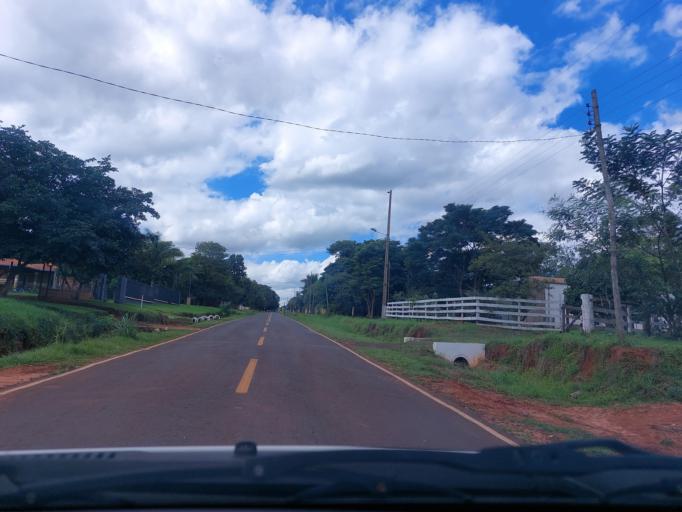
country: PY
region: San Pedro
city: Guayaybi
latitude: -24.5318
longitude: -56.5236
